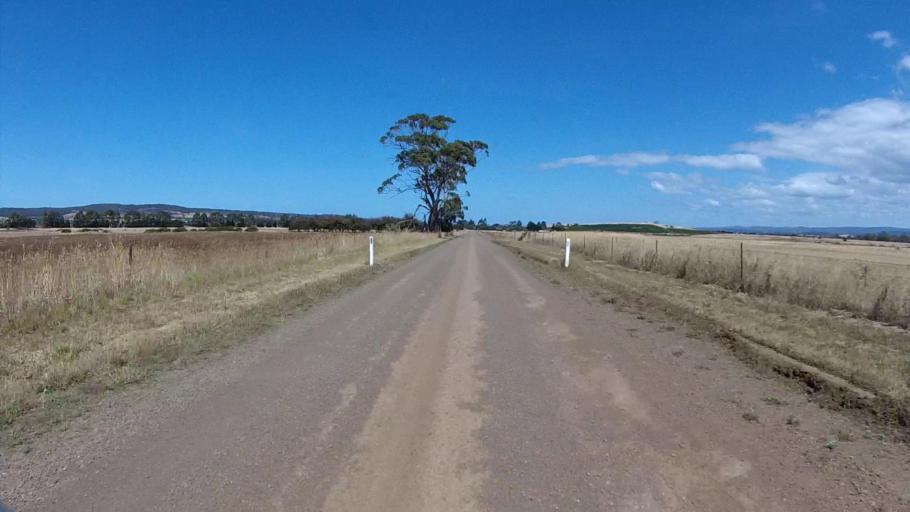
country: AU
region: Tasmania
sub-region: Break O'Day
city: St Helens
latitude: -41.9960
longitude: 148.0672
